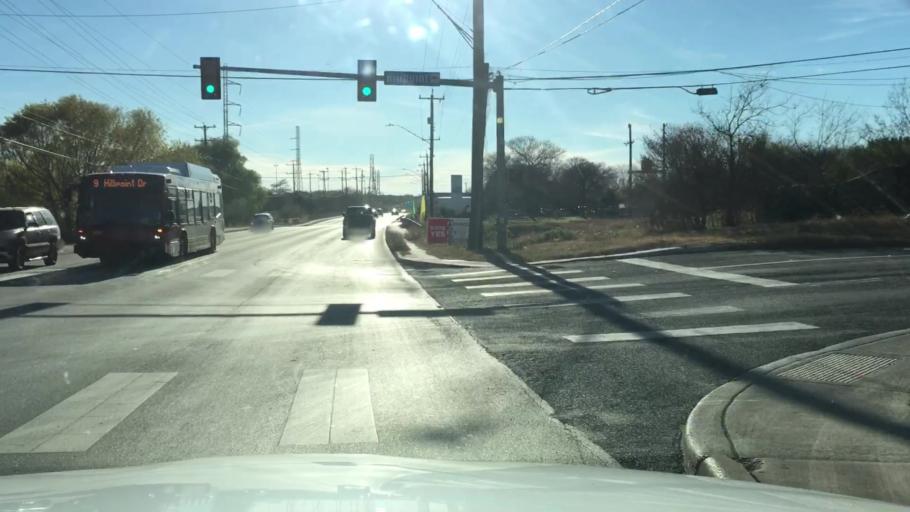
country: US
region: Texas
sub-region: Bexar County
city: Windcrest
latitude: 29.5376
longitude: -98.4246
